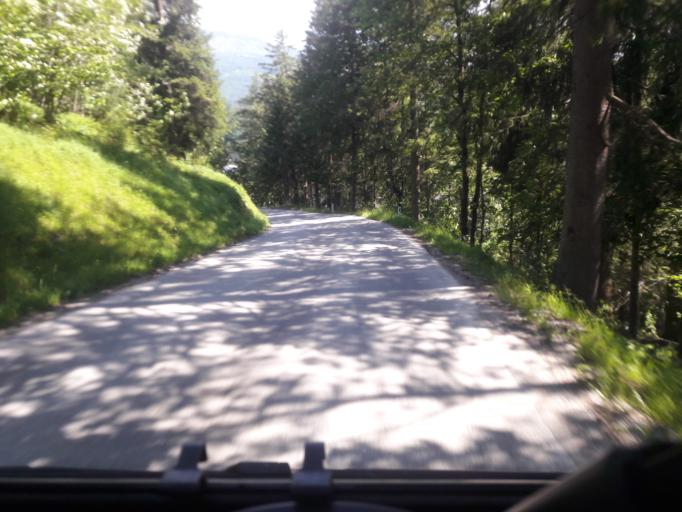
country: AT
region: Styria
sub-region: Politischer Bezirk Liezen
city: Tauplitz
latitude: 47.5559
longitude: 13.9433
